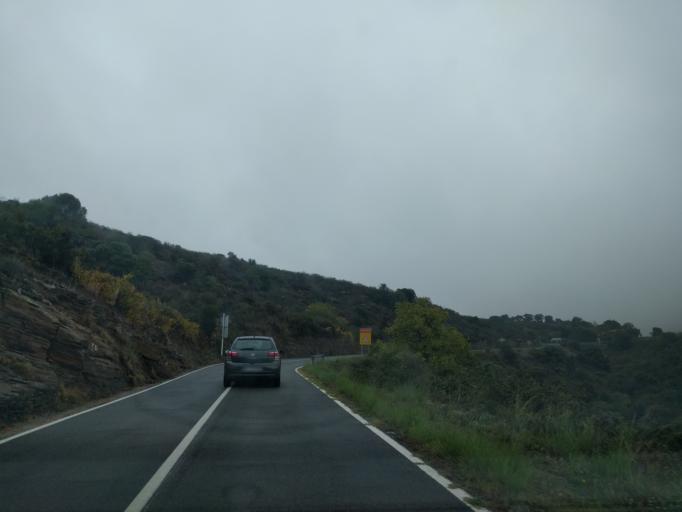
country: ES
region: Catalonia
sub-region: Provincia de Girona
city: Cadaques
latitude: 42.2981
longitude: 3.2343
